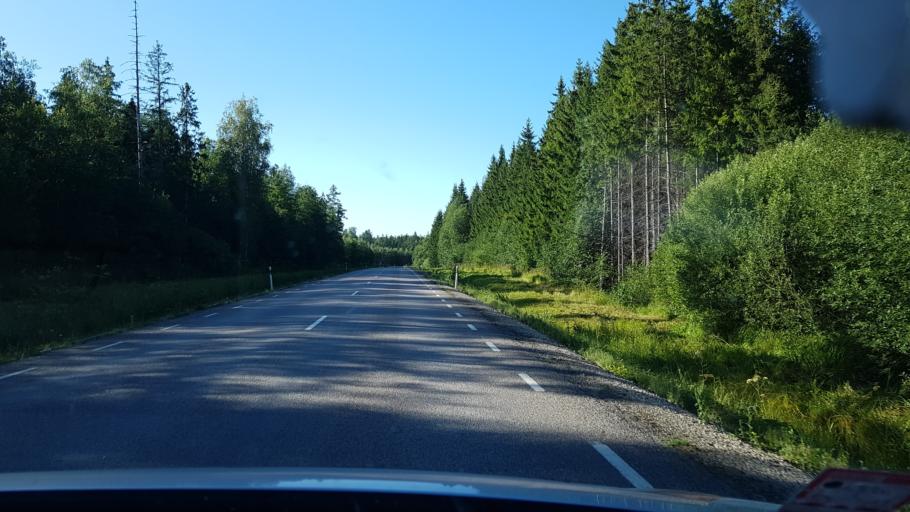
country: EE
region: Jogevamaa
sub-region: Mustvee linn
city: Mustvee
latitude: 59.0589
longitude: 27.0075
